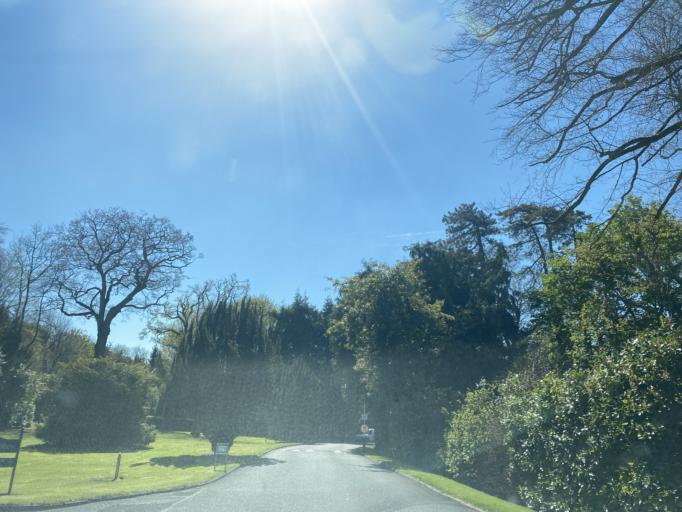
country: IE
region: Leinster
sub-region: Kildare
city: Monasterevin
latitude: 53.1377
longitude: -7.0629
